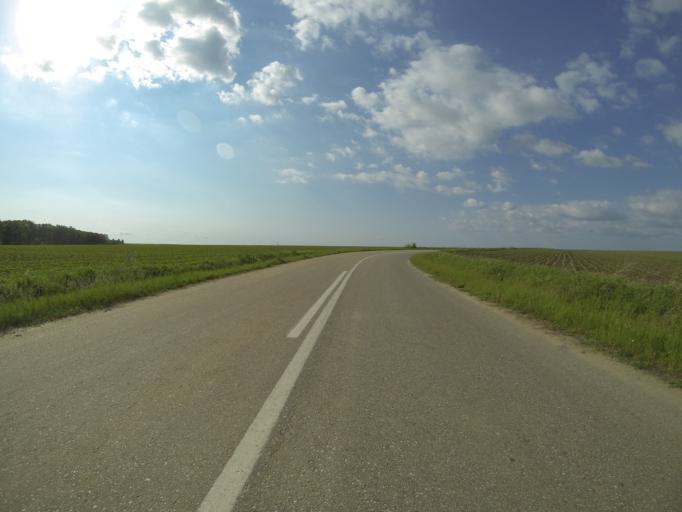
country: RO
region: Dolj
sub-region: Comuna Plenita
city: Castrele Traiane
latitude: 44.2552
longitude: 23.1501
